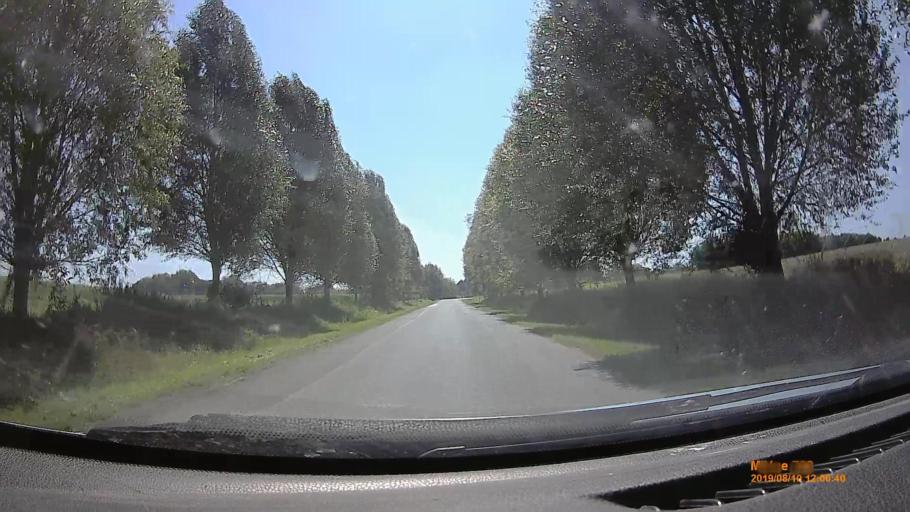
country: HU
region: Somogy
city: Somogyvar
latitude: 46.5769
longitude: 17.6766
